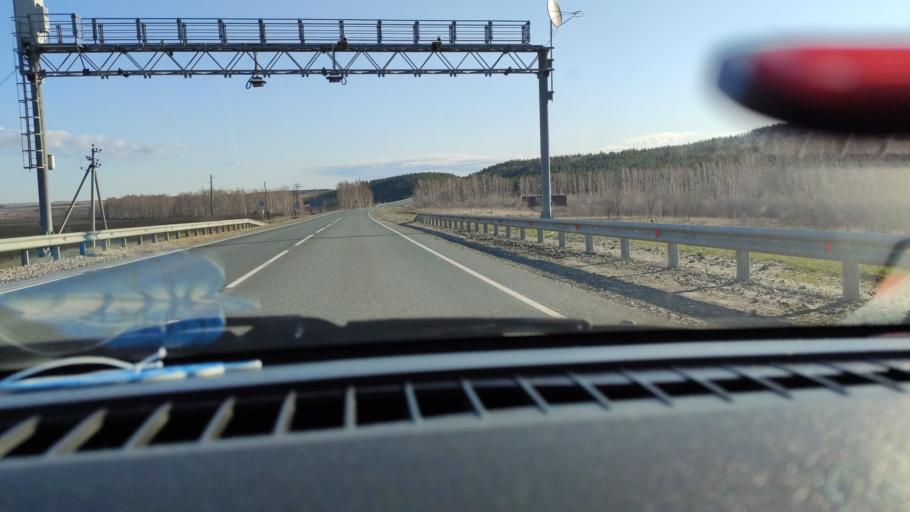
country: RU
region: Saratov
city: Khvalynsk
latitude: 52.5262
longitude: 48.0239
